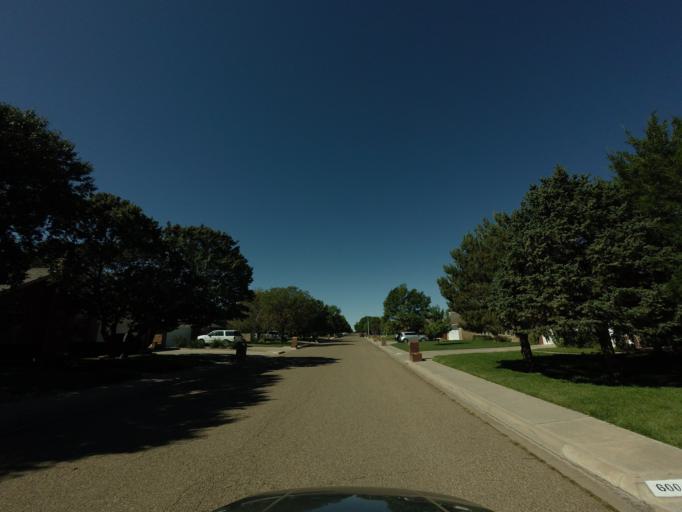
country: US
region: New Mexico
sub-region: Curry County
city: Clovis
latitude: 34.4215
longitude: -103.1713
